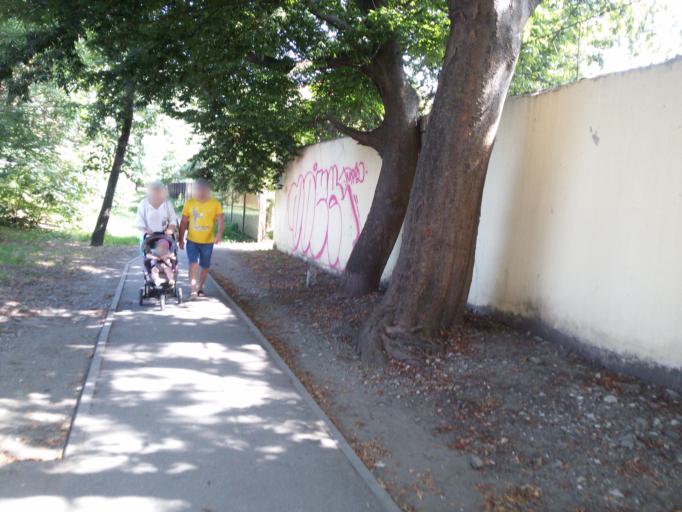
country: RU
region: Krasnodarskiy
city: Adler
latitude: 43.4226
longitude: 39.9356
